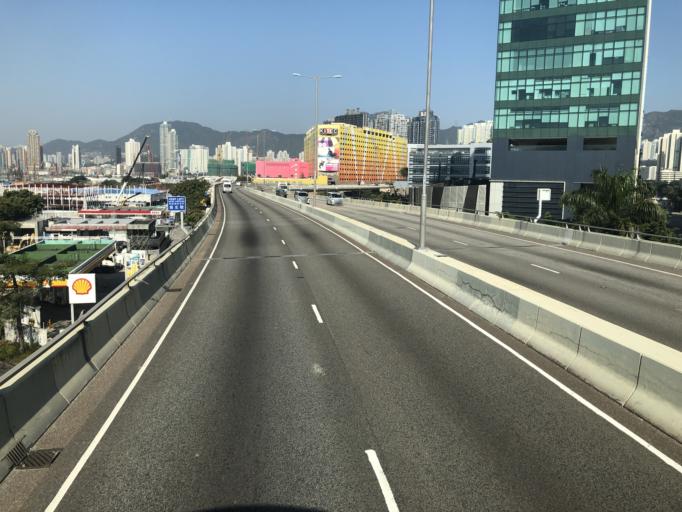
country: HK
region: Kowloon City
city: Kowloon
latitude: 22.3201
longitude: 114.2064
